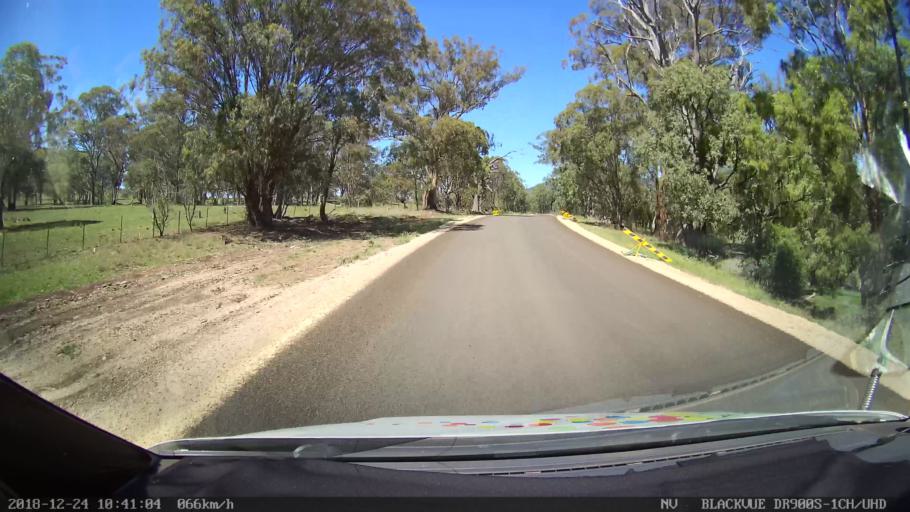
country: AU
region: New South Wales
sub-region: Upper Hunter Shire
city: Merriwa
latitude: -31.8664
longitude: 150.4624
